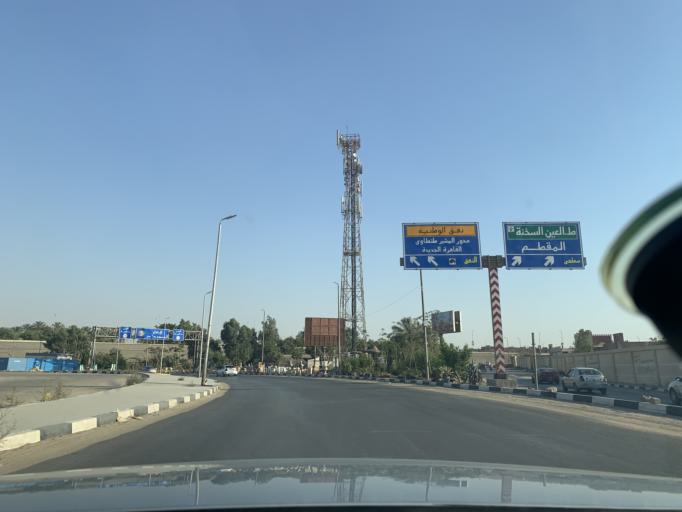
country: EG
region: Muhafazat al Qahirah
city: Cairo
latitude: 30.0249
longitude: 31.3537
